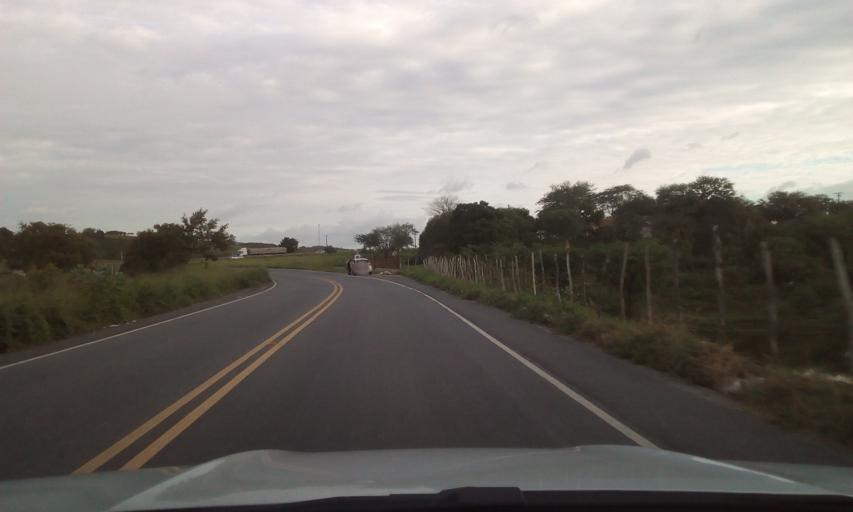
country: BR
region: Paraiba
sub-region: Serra Redonda
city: Alagoa Grande
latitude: -7.2140
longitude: -35.5935
